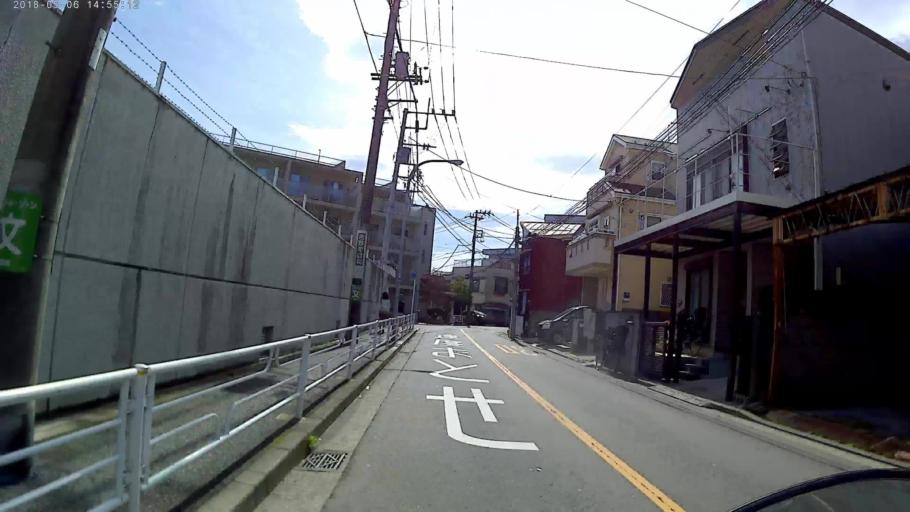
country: JP
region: Kanagawa
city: Yokohama
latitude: 35.4222
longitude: 139.6206
